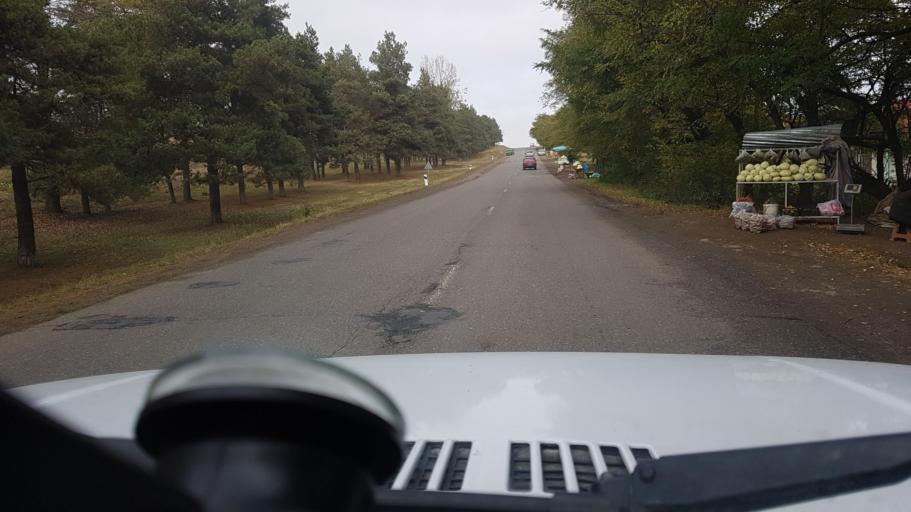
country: AZ
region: Gadabay Rayon
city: Ariqdam
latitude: 40.6356
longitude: 45.8131
